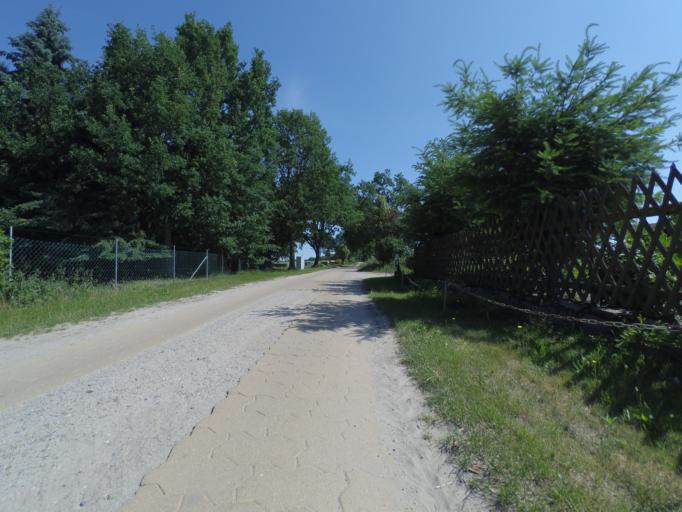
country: DE
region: Brandenburg
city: Pritzwalk
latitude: 53.1205
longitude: 12.2295
